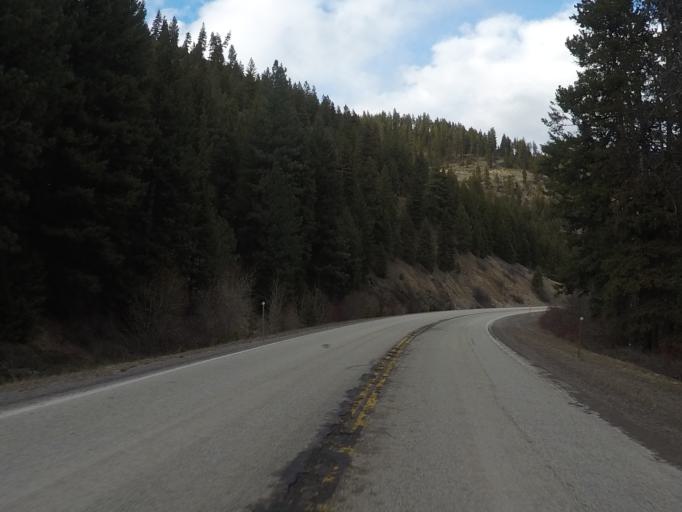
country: US
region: Montana
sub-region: Missoula County
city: Frenchtown
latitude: 46.7584
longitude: -114.4940
